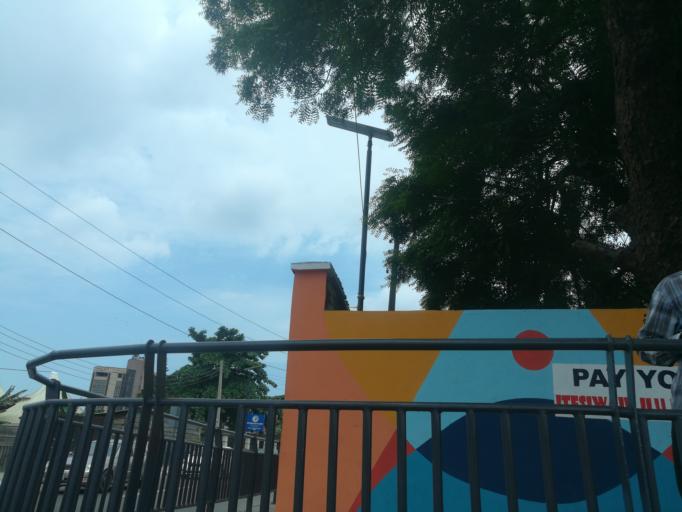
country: NG
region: Lagos
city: Ojota
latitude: 6.5754
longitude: 3.3685
